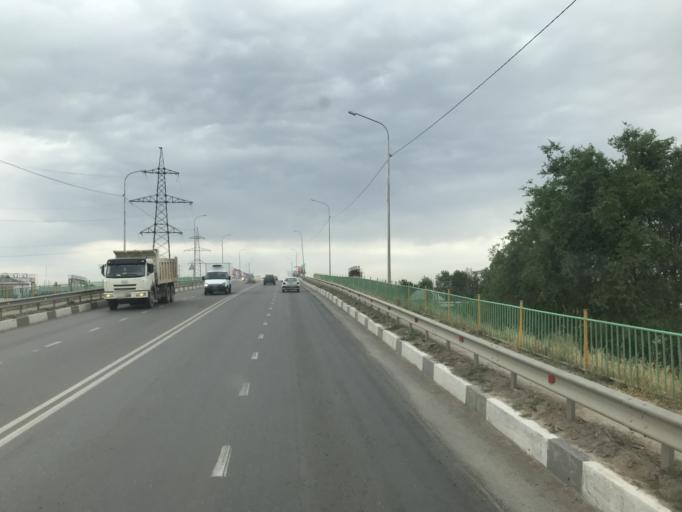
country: KZ
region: Ongtustik Qazaqstan
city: Saryaghash
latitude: 41.4610
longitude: 69.1494
